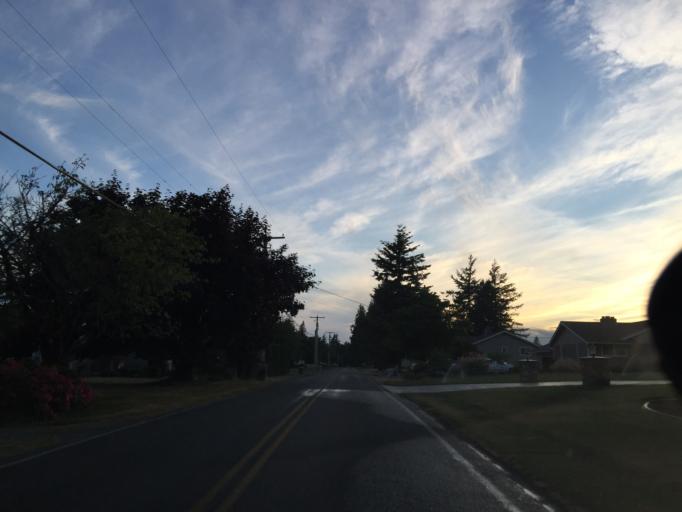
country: US
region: Washington
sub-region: Whatcom County
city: Lynden
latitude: 48.9567
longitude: -122.4127
